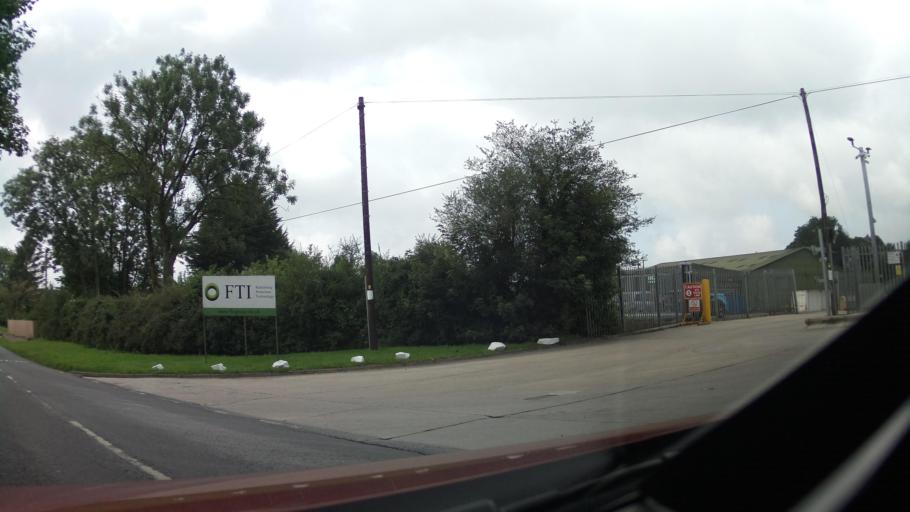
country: GB
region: England
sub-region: Somerset
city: Evercreech
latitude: 51.1993
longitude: -2.4891
